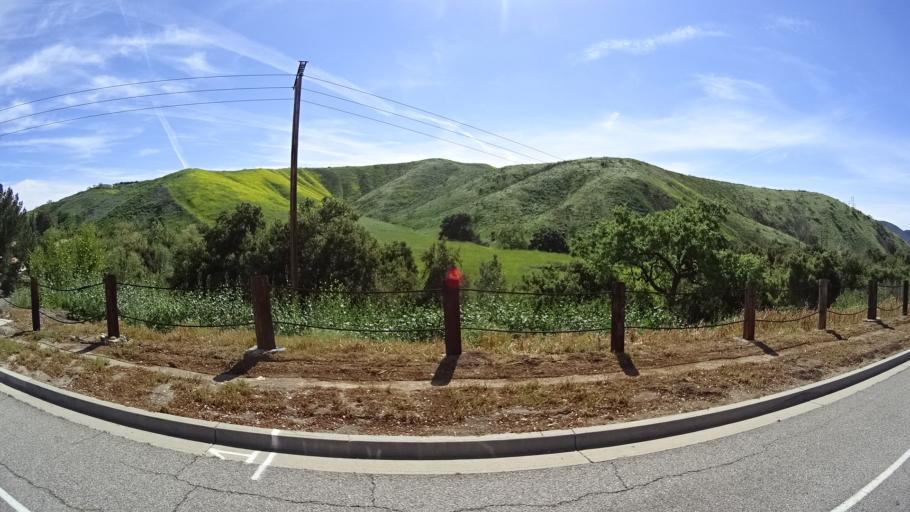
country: US
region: California
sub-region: Ventura County
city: Oak Park
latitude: 34.1703
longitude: -118.7884
